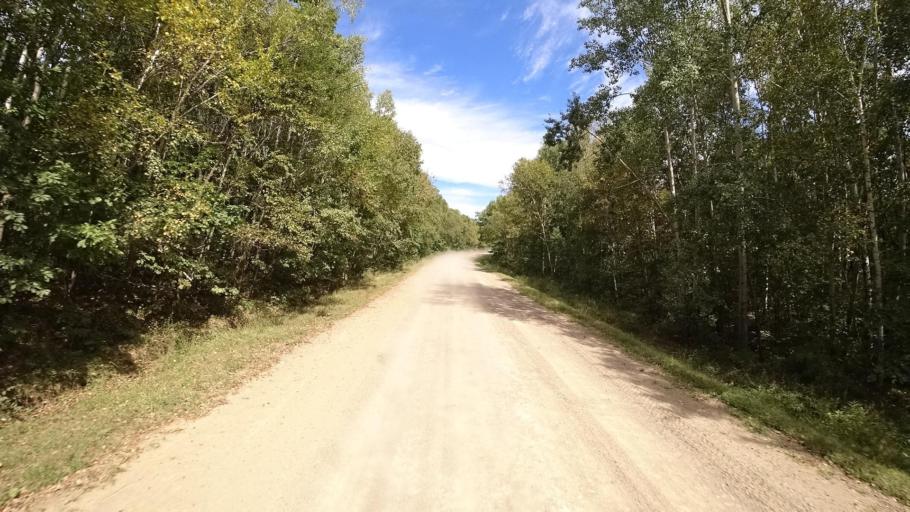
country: RU
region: Primorskiy
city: Yakovlevka
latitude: 44.6613
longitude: 133.5994
